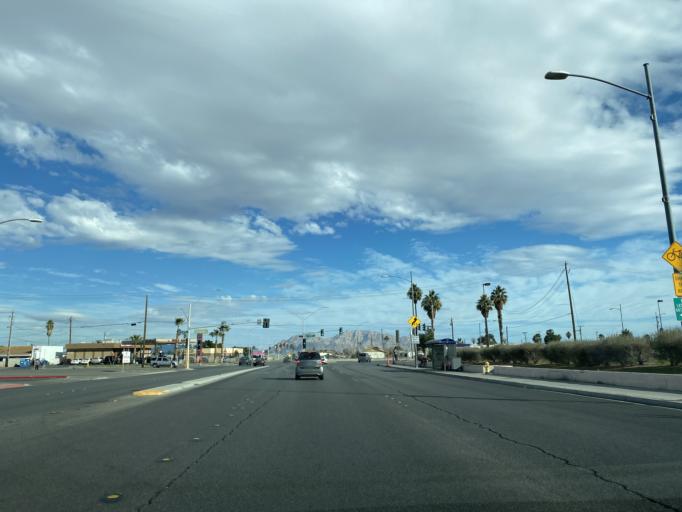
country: US
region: Nevada
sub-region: Clark County
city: Las Vegas
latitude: 36.1884
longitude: -115.1530
